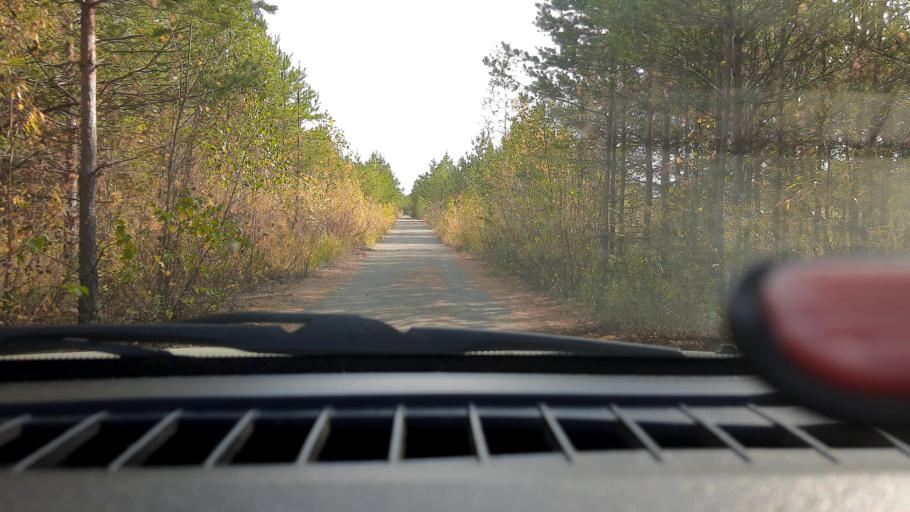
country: RU
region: Nizjnij Novgorod
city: Gorbatovka
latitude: 56.3565
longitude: 43.7620
